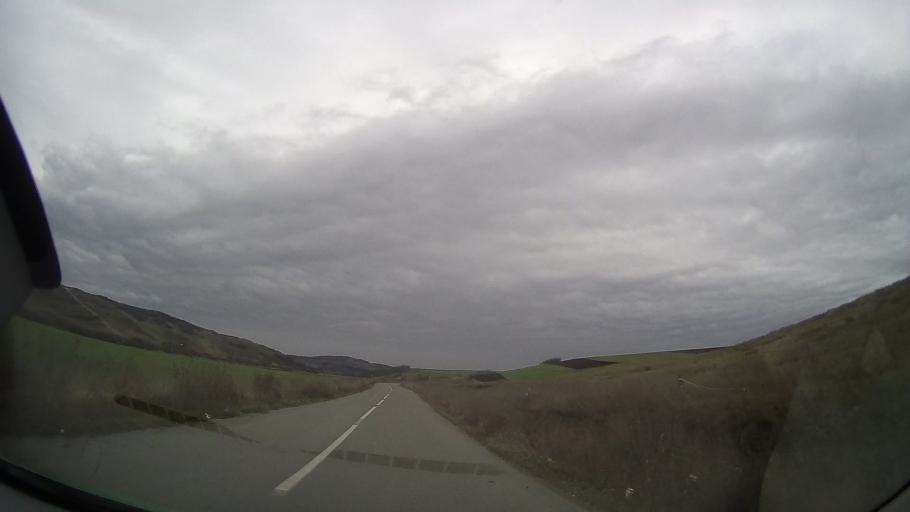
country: RO
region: Mures
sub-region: Comuna Craesti
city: Craiesti
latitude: 46.7796
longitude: 24.4258
